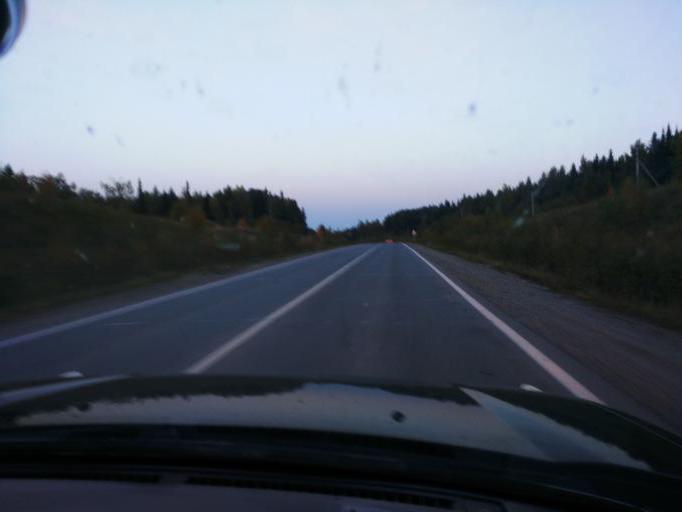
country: RU
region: Perm
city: Sylva
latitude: 58.2936
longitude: 56.8183
